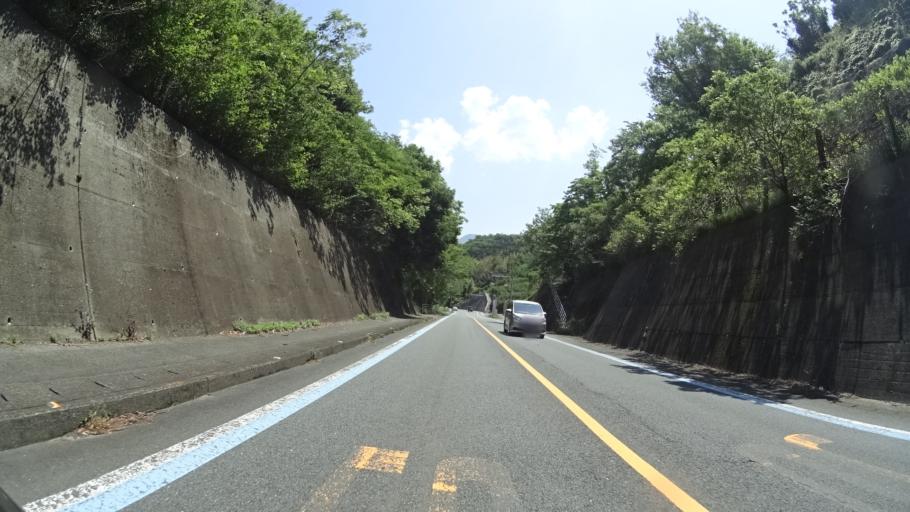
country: JP
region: Ehime
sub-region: Nishiuwa-gun
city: Ikata-cho
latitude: 33.4889
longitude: 132.3891
